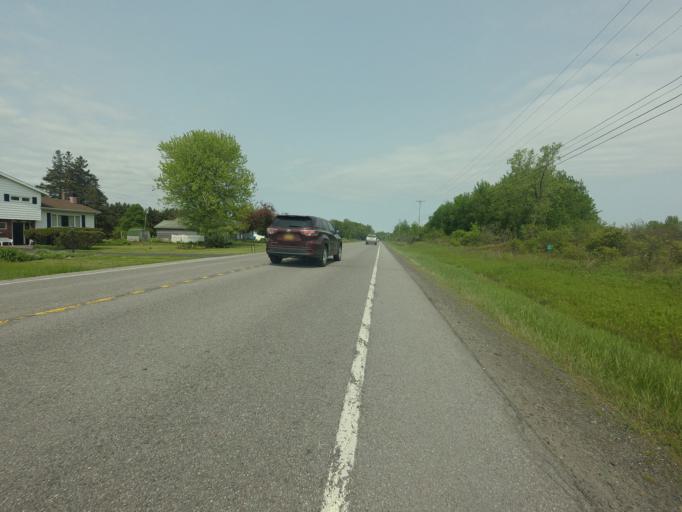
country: US
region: New York
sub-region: Jefferson County
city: Brownville
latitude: 44.0053
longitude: -76.0083
